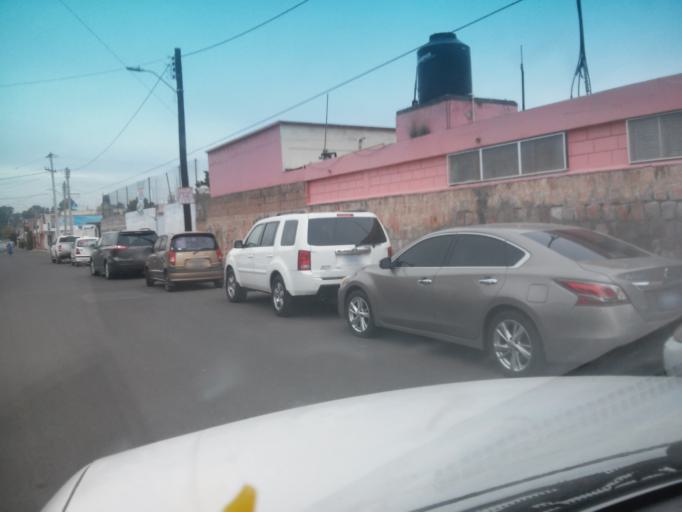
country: MX
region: Durango
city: Victoria de Durango
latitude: 24.0123
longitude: -104.6787
